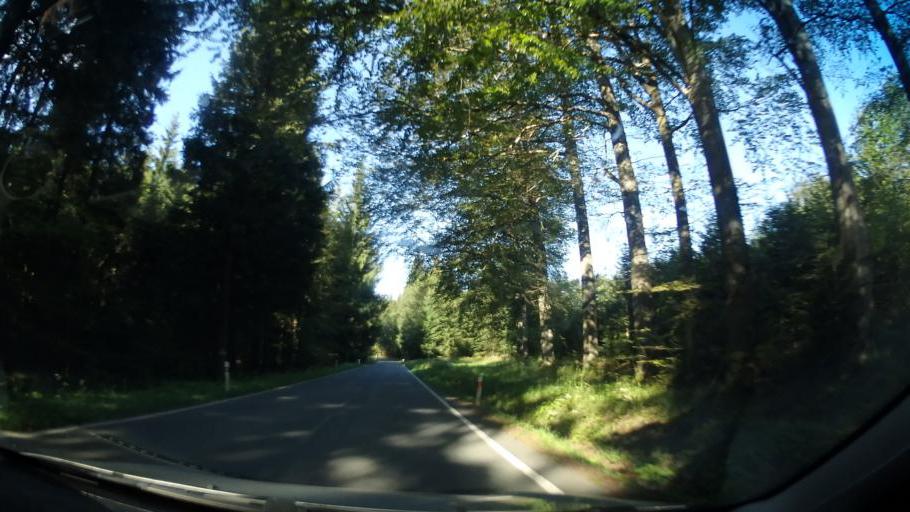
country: CZ
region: Olomoucky
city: Pisecna
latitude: 50.2285
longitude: 17.2897
